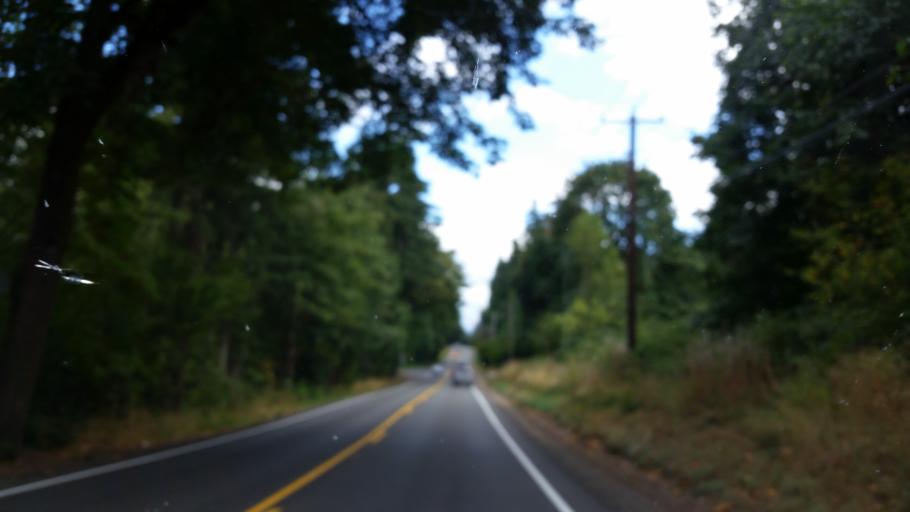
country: US
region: Washington
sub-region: Pierce County
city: Bonney Lake
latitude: 47.2459
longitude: -122.1508
